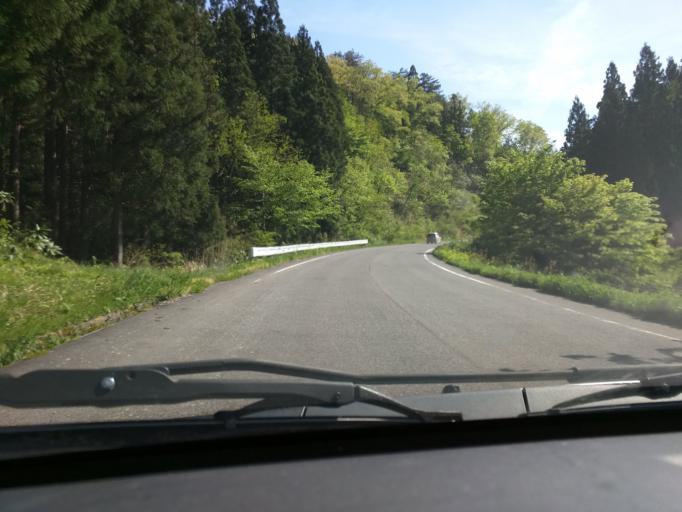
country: JP
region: Fukushima
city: Kitakata
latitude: 37.5681
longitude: 139.6352
